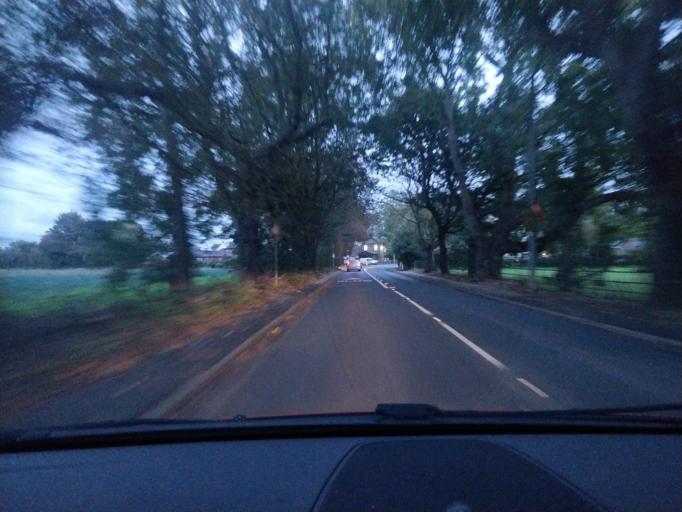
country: GB
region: England
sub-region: Lancashire
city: Ormskirk
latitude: 53.5976
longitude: -2.9241
